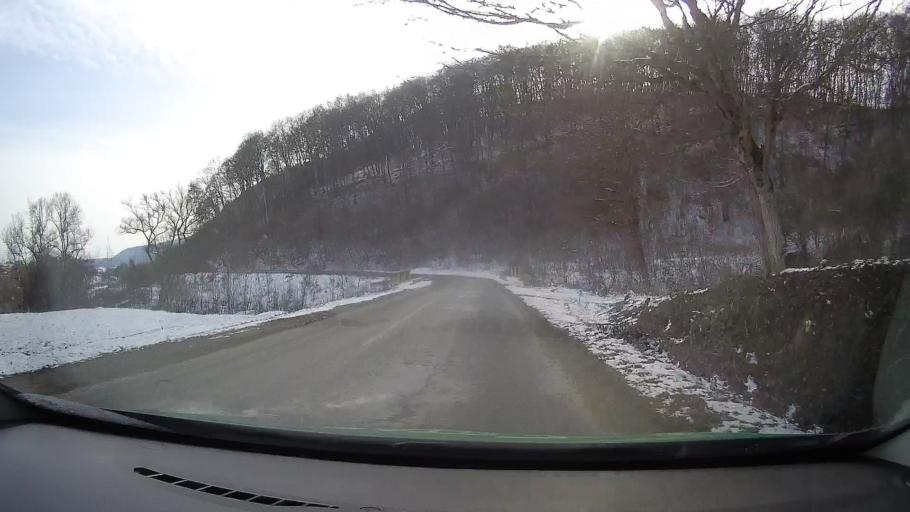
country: RO
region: Mures
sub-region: Comuna Apold
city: Saes
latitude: 46.1673
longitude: 24.7568
